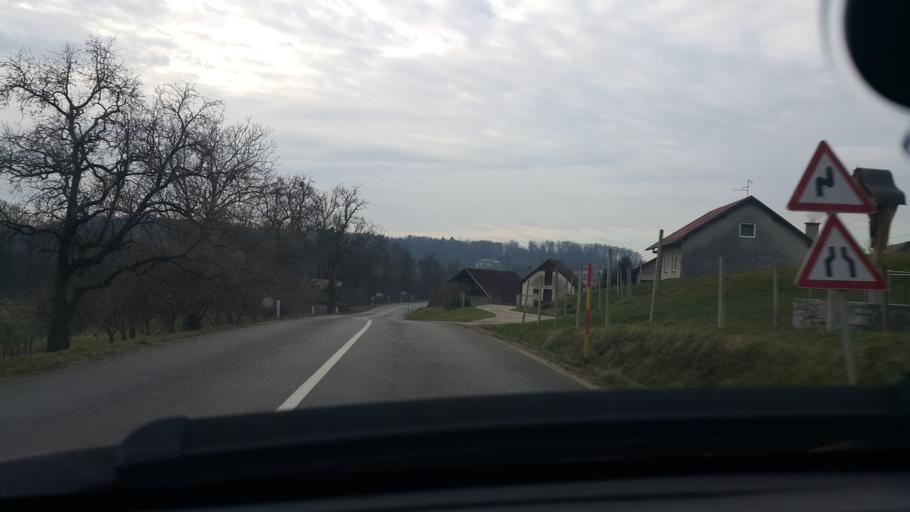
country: SI
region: Bistrica ob Sotli
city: Bistrica ob Sotli
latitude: 45.9666
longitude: 15.6934
